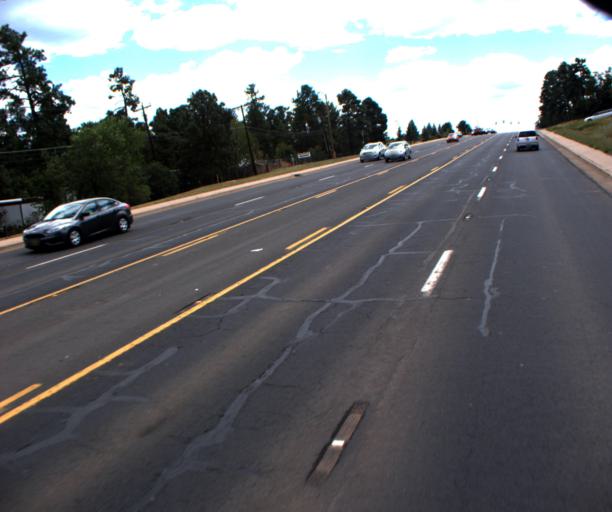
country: US
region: Arizona
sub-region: Navajo County
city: Show Low
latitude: 34.2049
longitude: -110.0206
